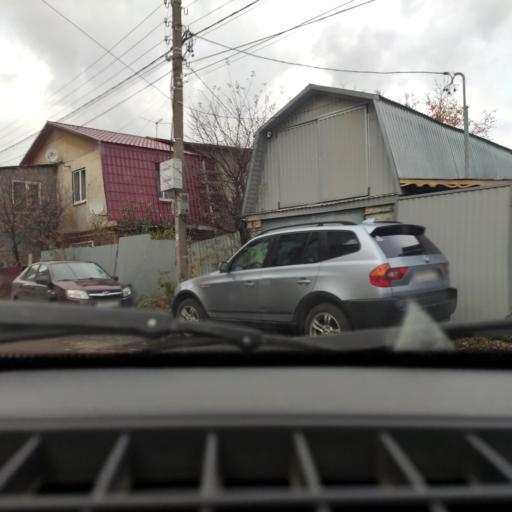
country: RU
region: Bashkortostan
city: Mikhaylovka
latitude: 54.7877
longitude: 55.8870
